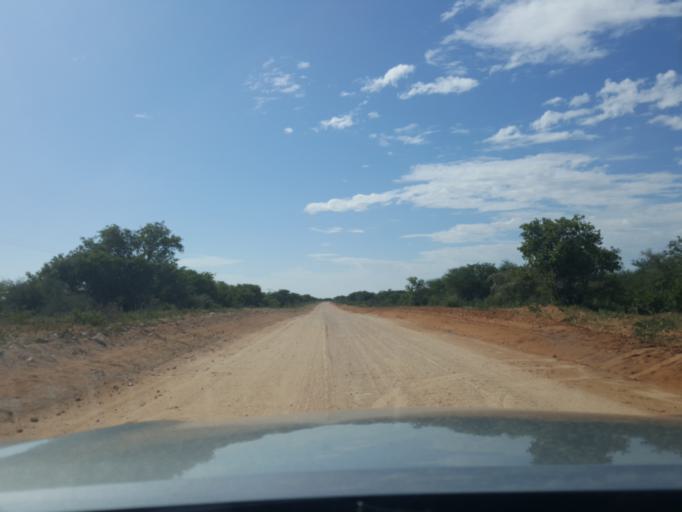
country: BW
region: Kweneng
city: Khudumelapye
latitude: -23.7691
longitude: 24.7656
